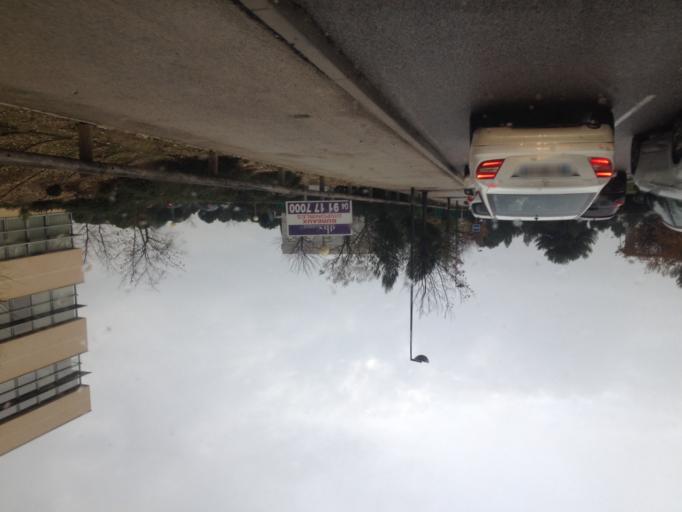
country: FR
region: Provence-Alpes-Cote d'Azur
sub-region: Departement des Bouches-du-Rhone
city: Cabries
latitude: 43.4956
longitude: 5.3483
